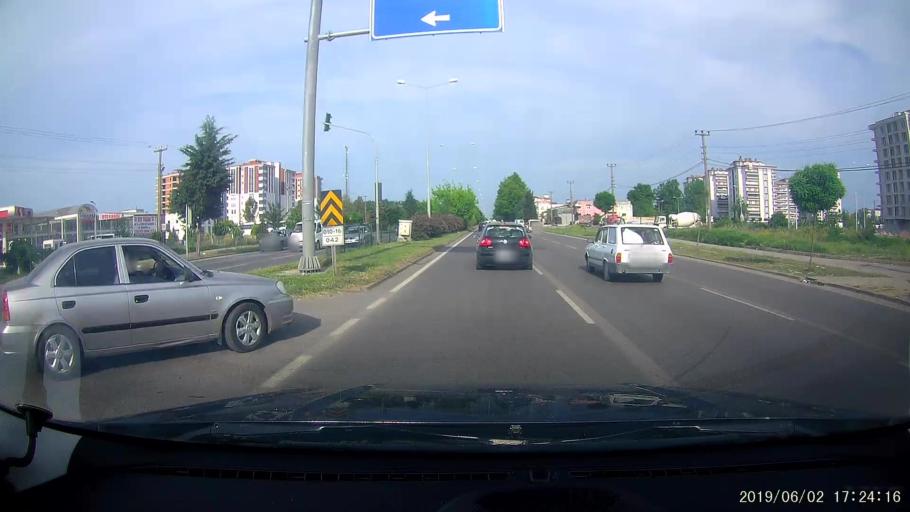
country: TR
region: Samsun
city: Carsamba
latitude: 41.2058
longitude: 36.6993
